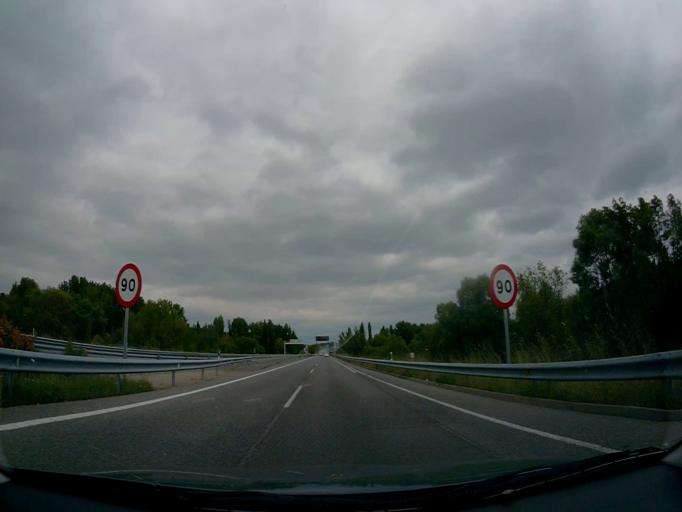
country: ES
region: Madrid
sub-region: Provincia de Madrid
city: Villaviciosa de Odon
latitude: 40.3666
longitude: -3.9465
